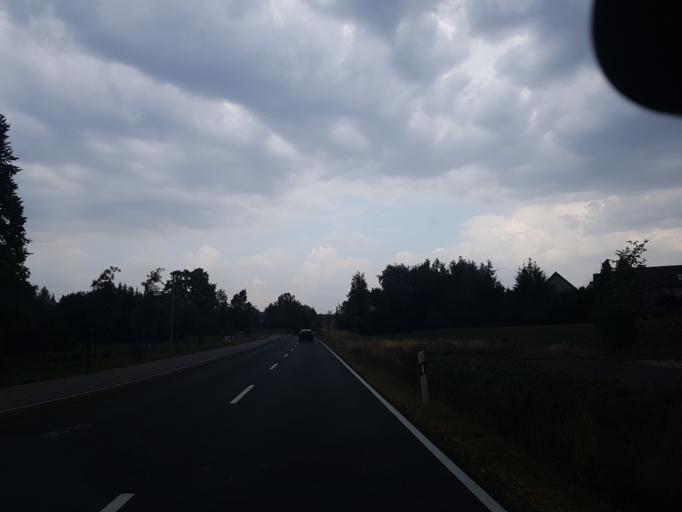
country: DE
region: Saxony
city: Ebersbach
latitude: 51.0902
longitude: 13.0878
